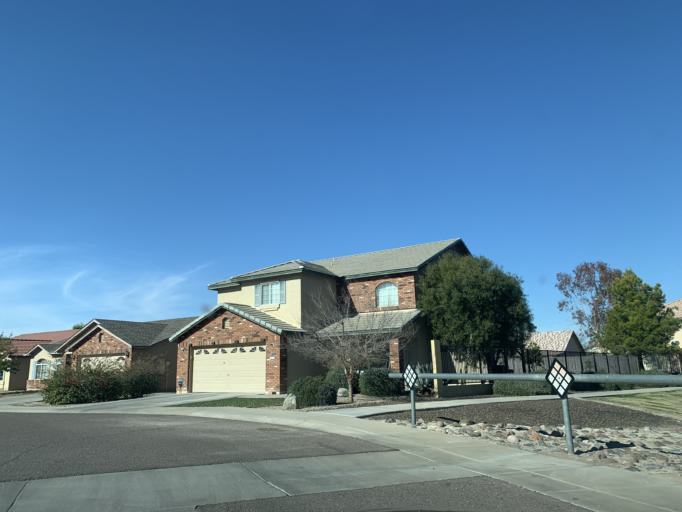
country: US
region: Arizona
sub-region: Maricopa County
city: Laveen
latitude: 33.3942
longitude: -112.1217
